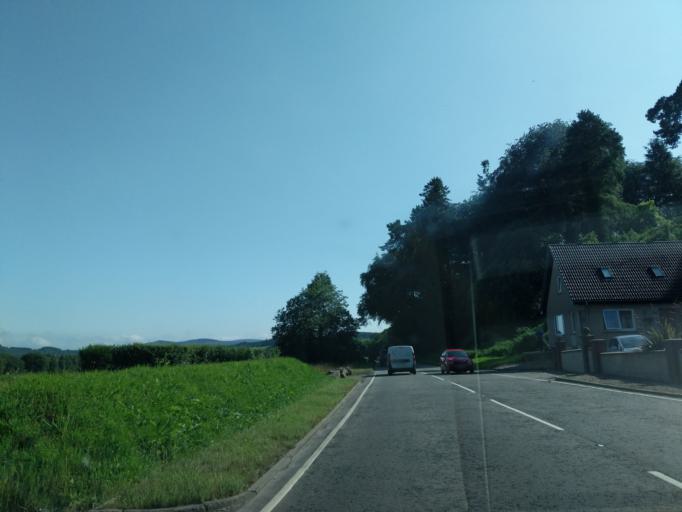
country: GB
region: Scotland
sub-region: Moray
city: Rothes
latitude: 57.5201
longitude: -3.2094
